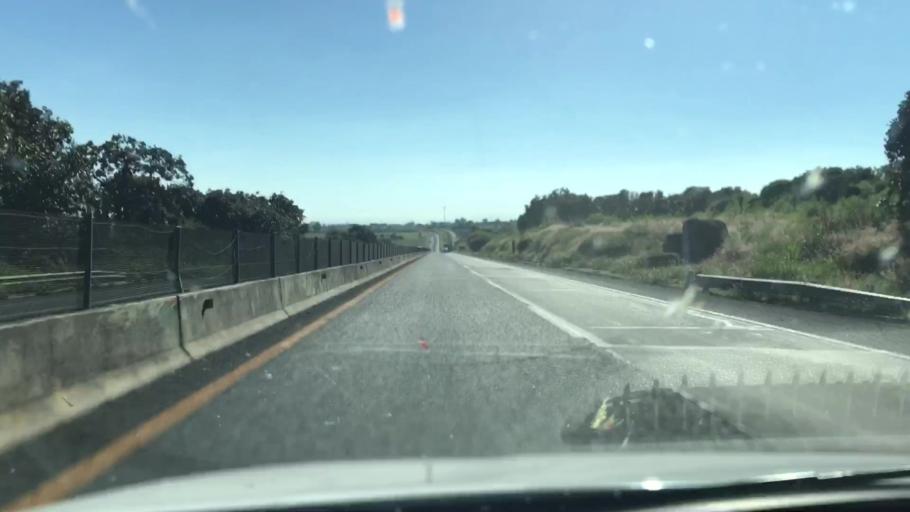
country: MX
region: Jalisco
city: Tepatitlan de Morelos
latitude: 20.8547
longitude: -102.7712
